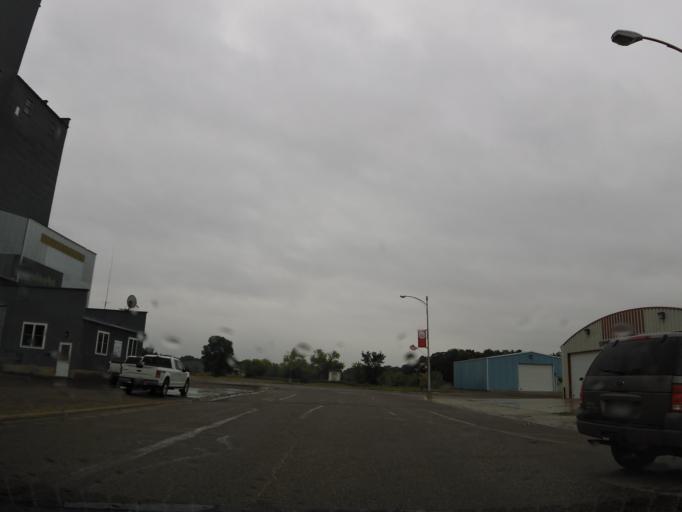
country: US
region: Minnesota
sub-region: Marshall County
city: Warren
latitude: 48.4498
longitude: -96.8741
